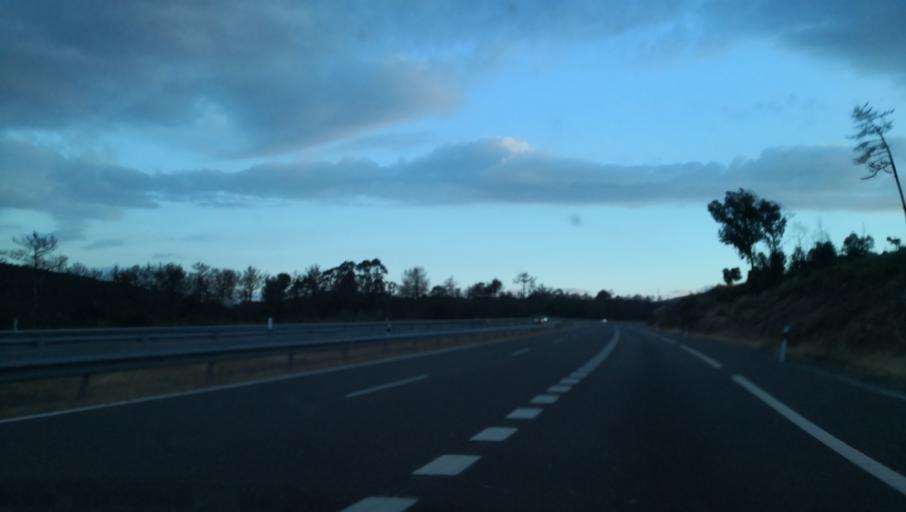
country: ES
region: Galicia
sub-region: Provincia de Ourense
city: Carballeda de Avia
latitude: 42.2964
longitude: -8.1873
